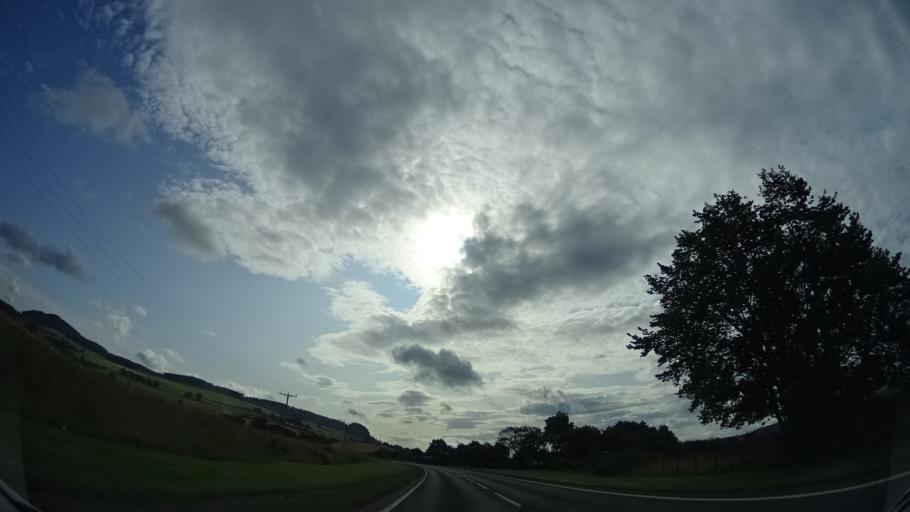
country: GB
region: Scotland
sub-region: Highland
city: Muir of Ord
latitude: 57.5613
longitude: -4.5638
